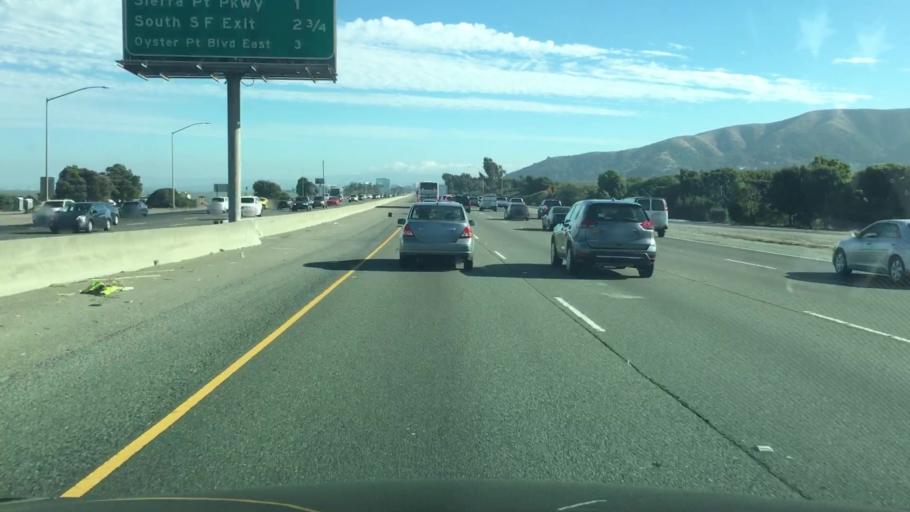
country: US
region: California
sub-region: San Mateo County
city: Brisbane
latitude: 37.7065
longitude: -122.3939
